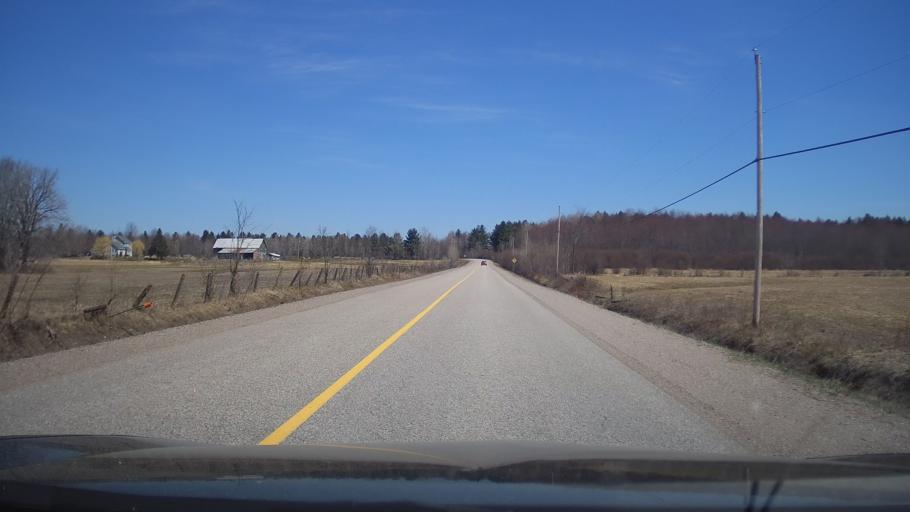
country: CA
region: Ontario
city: Arnprior
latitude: 45.5393
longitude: -76.3677
